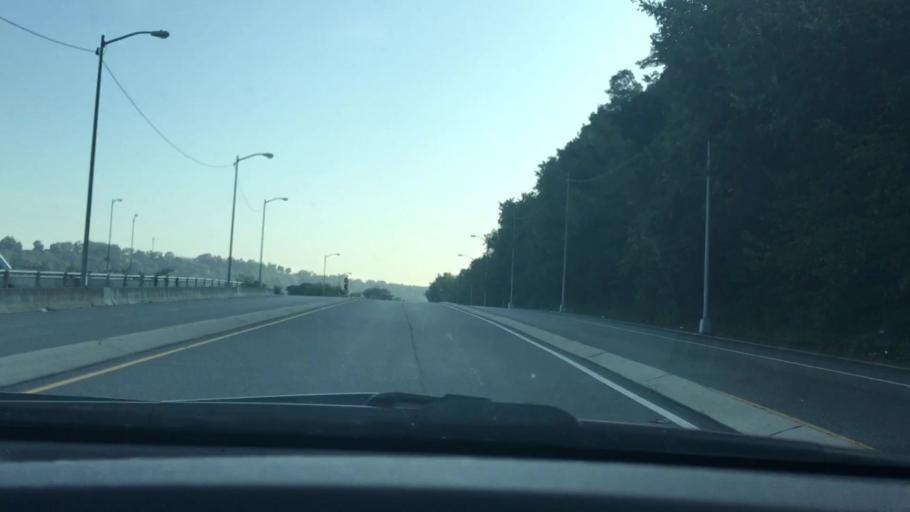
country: US
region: Pennsylvania
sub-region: Allegheny County
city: Dravosburg
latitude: 40.3435
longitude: -79.8847
